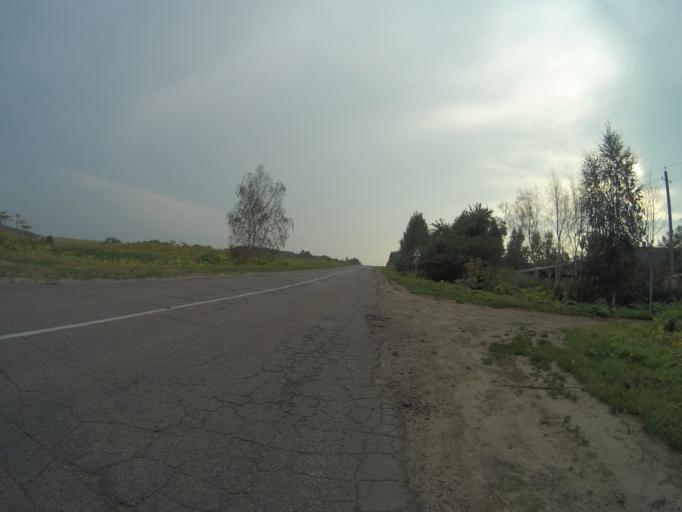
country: RU
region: Ivanovo
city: Gavrilov Posad
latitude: 56.3465
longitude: 40.1487
